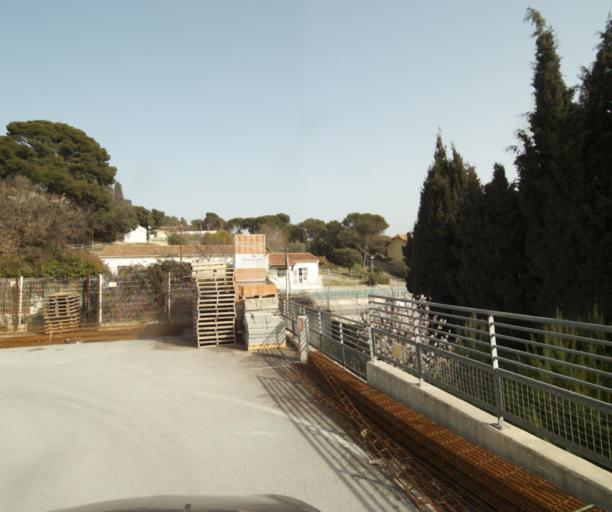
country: FR
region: Provence-Alpes-Cote d'Azur
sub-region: Departement des Bouches-du-Rhone
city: Septemes-les-Vallons
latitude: 43.3962
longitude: 5.3423
